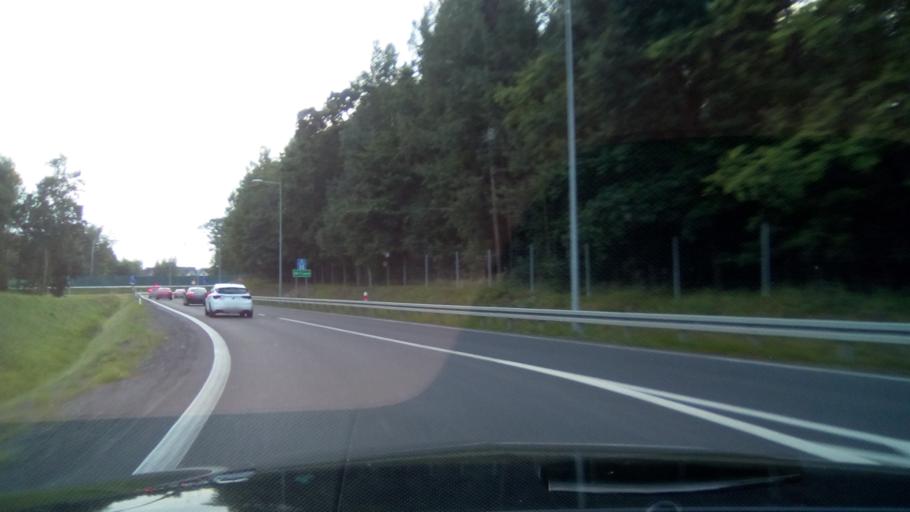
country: PL
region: Silesian Voivodeship
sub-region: Myslowice
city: Myslowice
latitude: 50.2193
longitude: 19.1264
